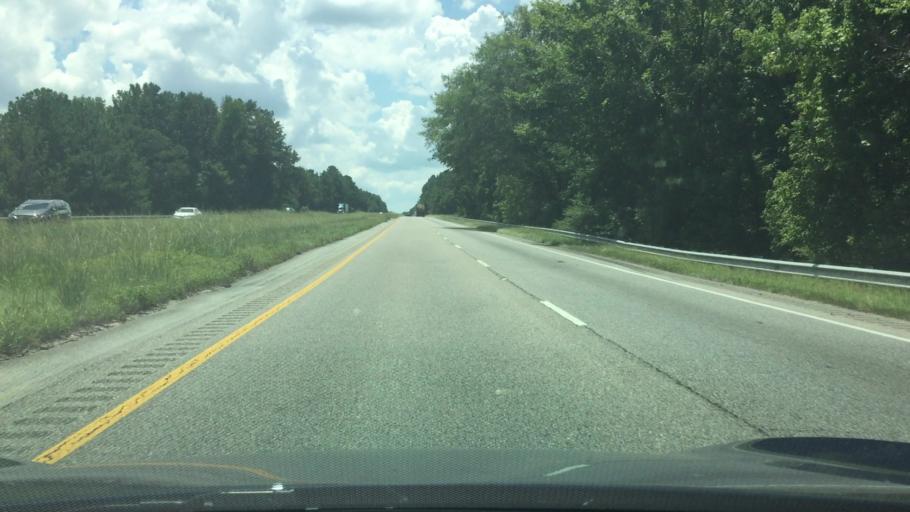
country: US
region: Alabama
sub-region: Montgomery County
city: Pike Road
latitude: 32.0909
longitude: -86.0646
